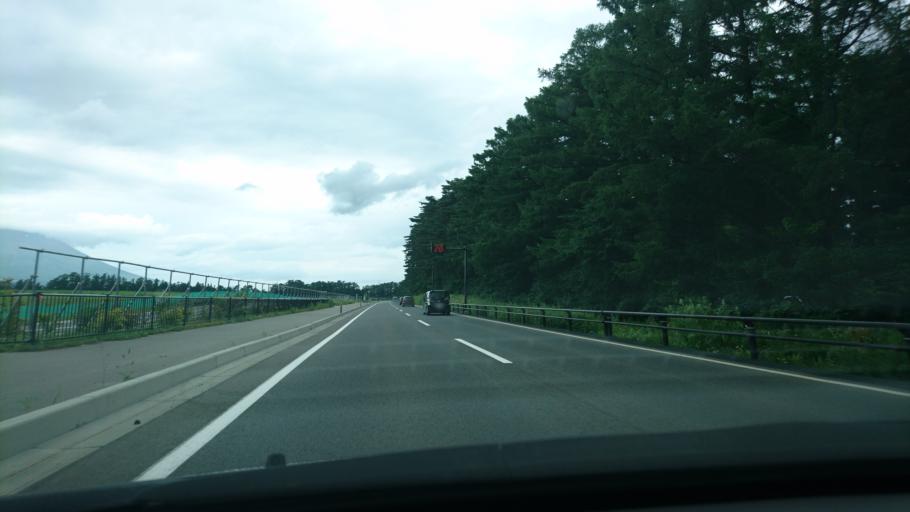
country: JP
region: Iwate
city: Morioka-shi
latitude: 39.7621
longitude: 141.1324
